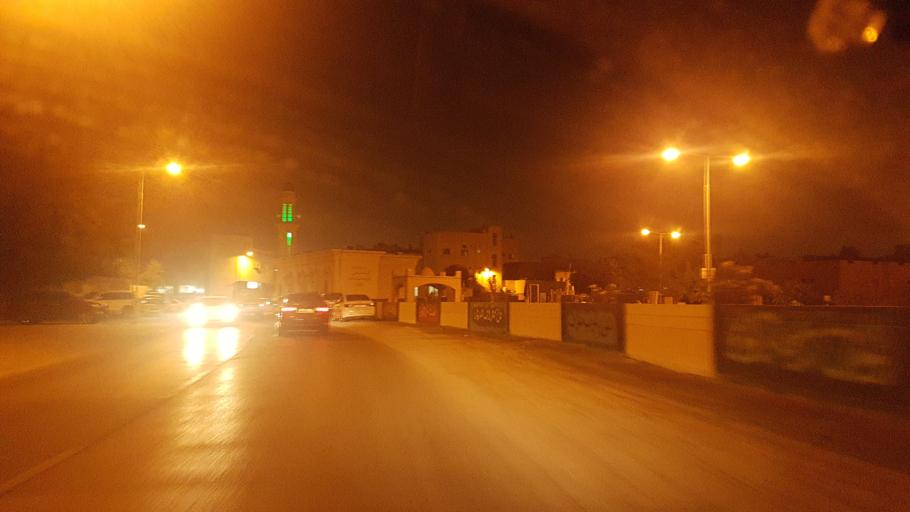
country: BH
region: Manama
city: Jidd Hafs
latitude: 26.2273
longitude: 50.5161
